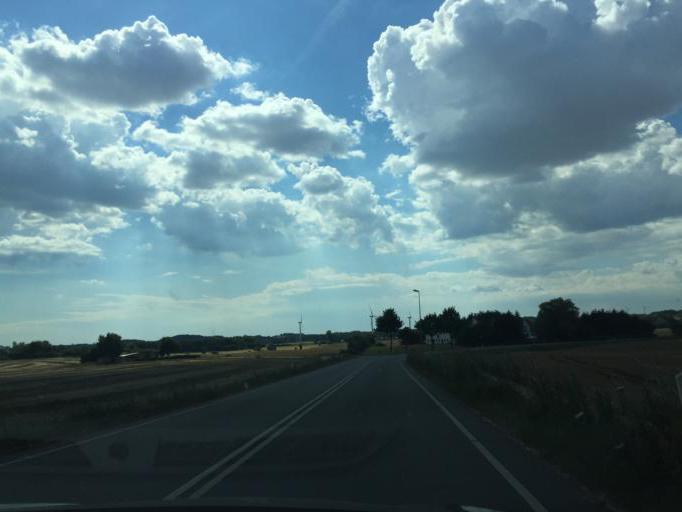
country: DK
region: South Denmark
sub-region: Assens Kommune
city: Harby
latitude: 55.2218
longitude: 10.1098
